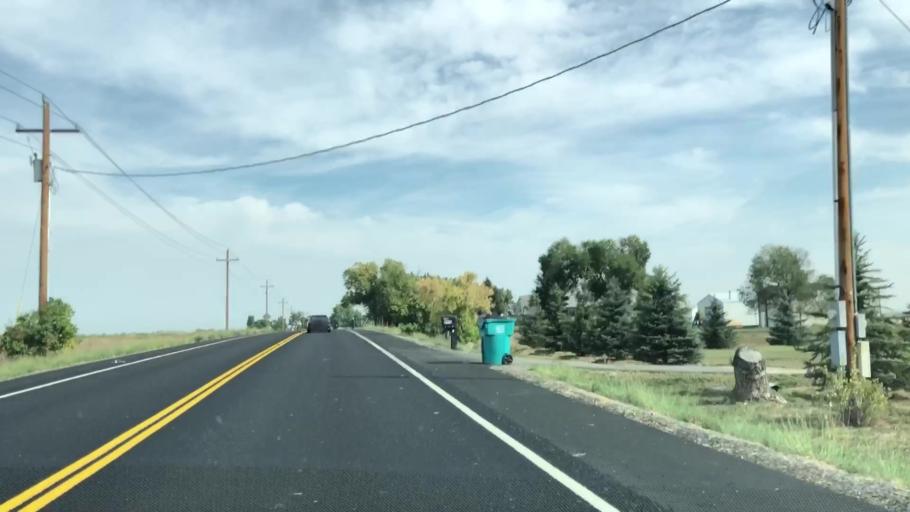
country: US
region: Colorado
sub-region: Larimer County
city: Loveland
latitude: 40.4680
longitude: -105.0395
